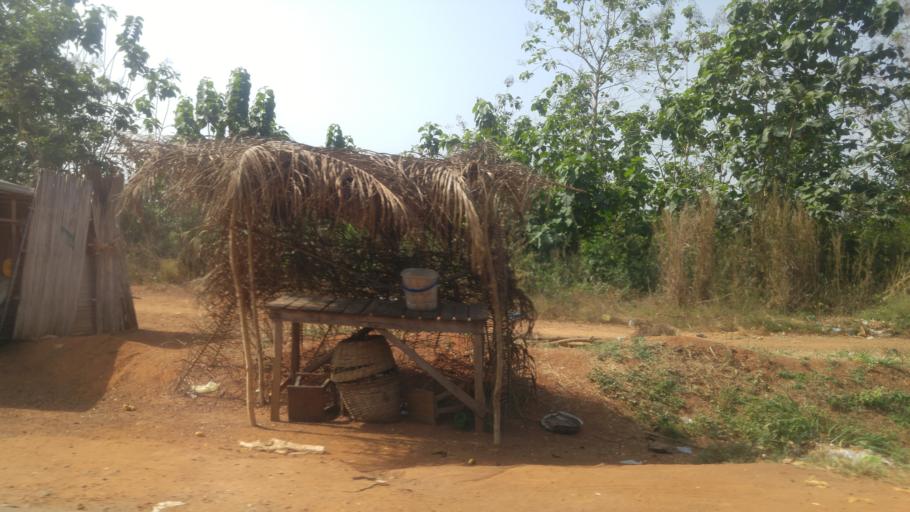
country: BJ
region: Zou
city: Bohicon
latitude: 7.0213
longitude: 2.1791
